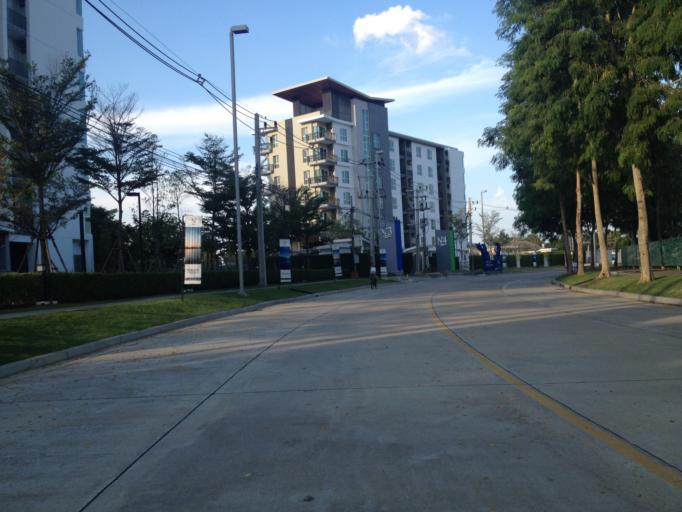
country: TH
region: Chiang Mai
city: Chiang Mai
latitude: 18.7593
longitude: 98.9502
